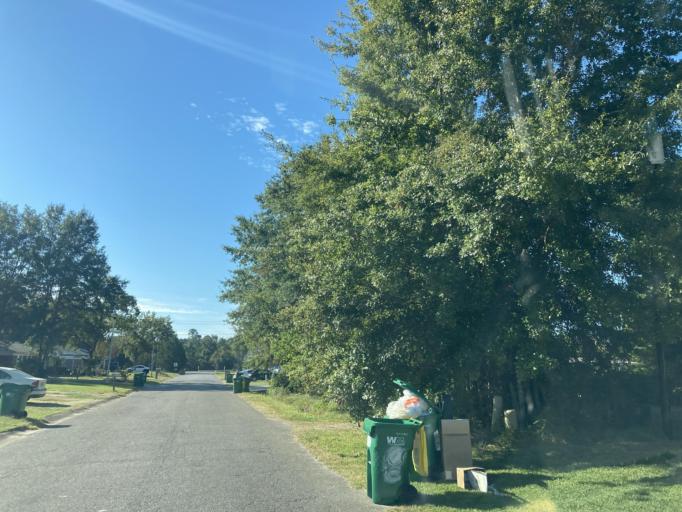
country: US
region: Mississippi
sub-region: Jackson County
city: Saint Martin
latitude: 30.4399
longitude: -88.8798
